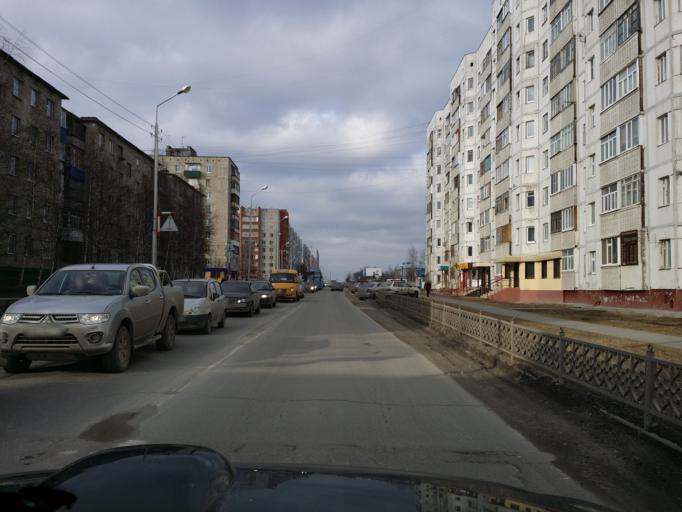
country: RU
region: Khanty-Mansiyskiy Avtonomnyy Okrug
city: Nizhnevartovsk
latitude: 60.9413
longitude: 76.6083
